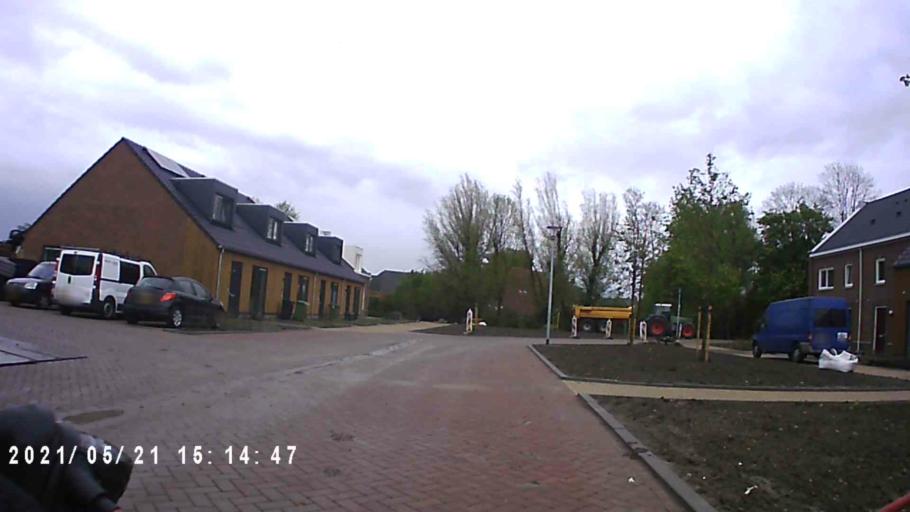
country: NL
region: Groningen
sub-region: Gemeente Zuidhorn
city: Aduard
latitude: 53.2580
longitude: 6.4562
